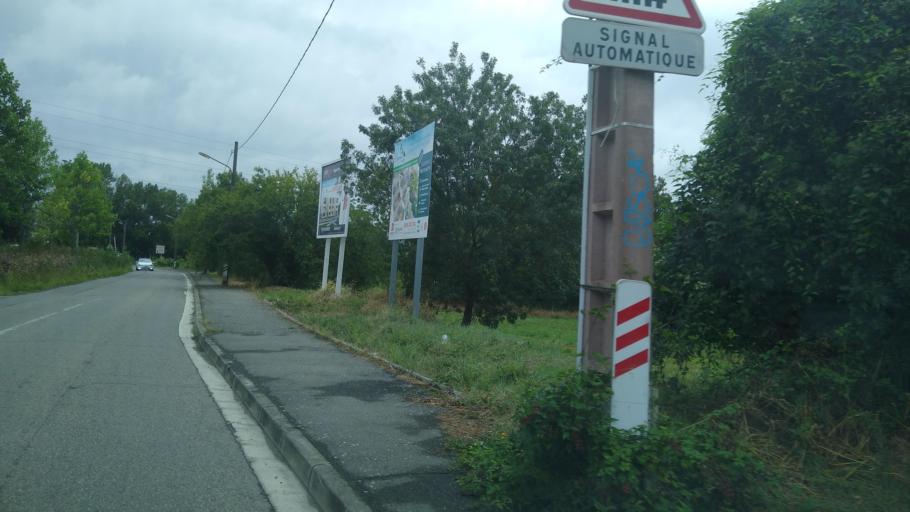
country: FR
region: Midi-Pyrenees
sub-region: Departement de la Haute-Garonne
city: Blagnac
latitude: 43.5985
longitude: 1.3714
